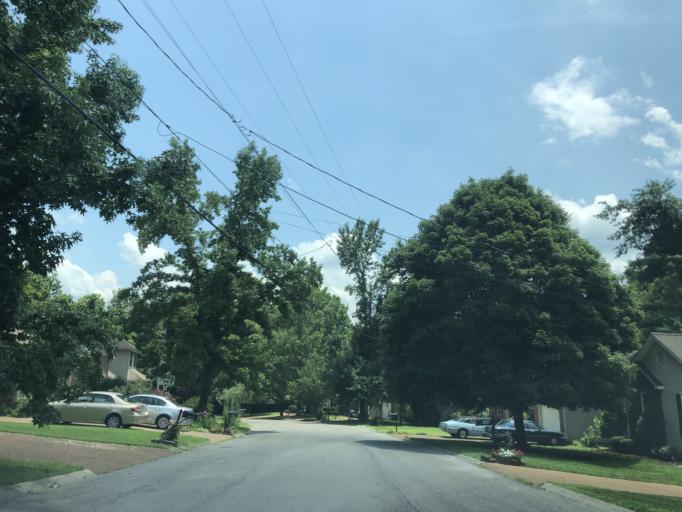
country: US
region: Tennessee
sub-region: Williamson County
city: Brentwood Estates
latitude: 36.0232
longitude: -86.7178
